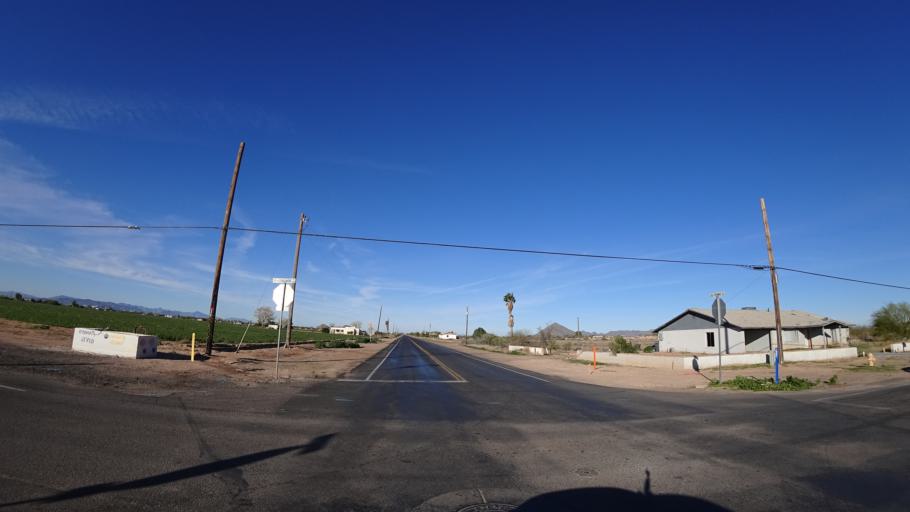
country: US
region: Arizona
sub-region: Maricopa County
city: Scottsdale
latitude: 33.4805
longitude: -111.8654
